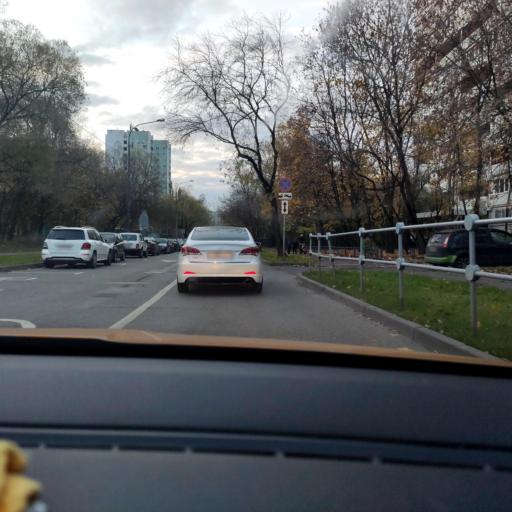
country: RU
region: Moscow
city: Gol'yanovo
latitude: 55.8149
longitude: 37.8207
